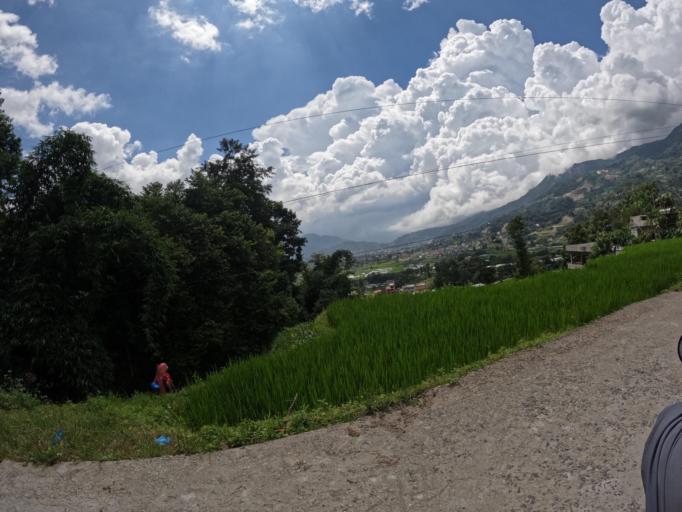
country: NP
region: Central Region
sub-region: Bagmati Zone
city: Kathmandu
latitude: 27.7885
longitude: 85.3316
